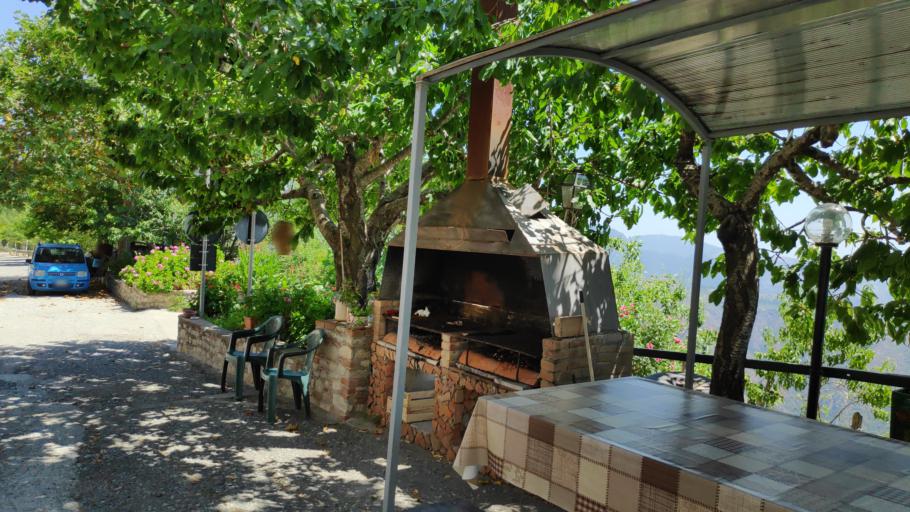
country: IT
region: Calabria
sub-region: Provincia di Reggio Calabria
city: Bova
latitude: 37.9951
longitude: 15.9345
